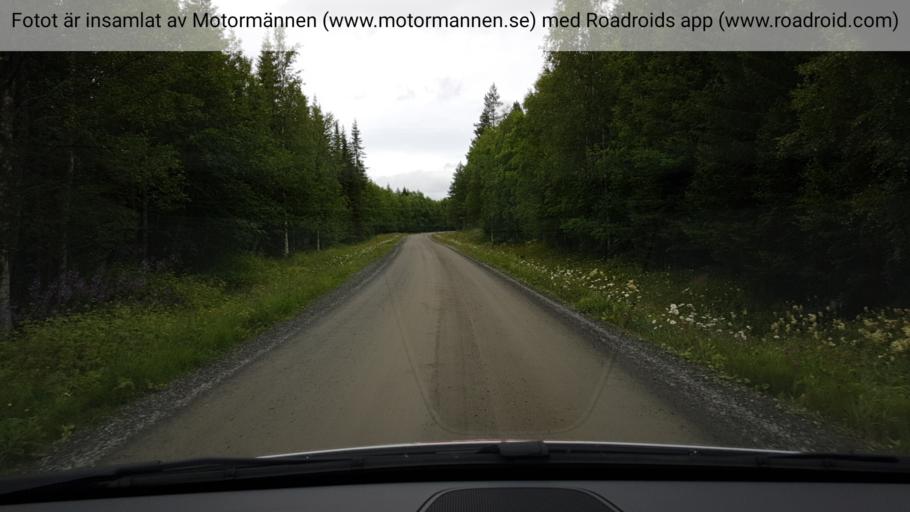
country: SE
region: Jaemtland
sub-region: Krokoms Kommun
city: Krokom
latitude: 63.7517
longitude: 14.4508
